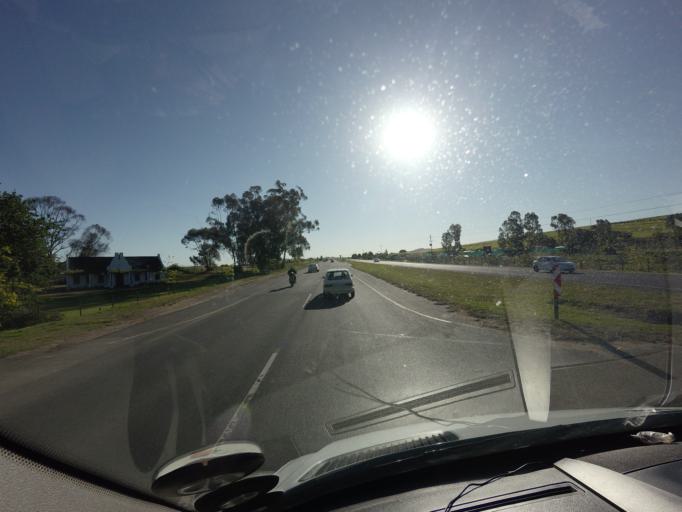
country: ZA
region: Western Cape
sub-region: Cape Winelands District Municipality
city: Stellenbosch
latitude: -33.9472
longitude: 18.8227
